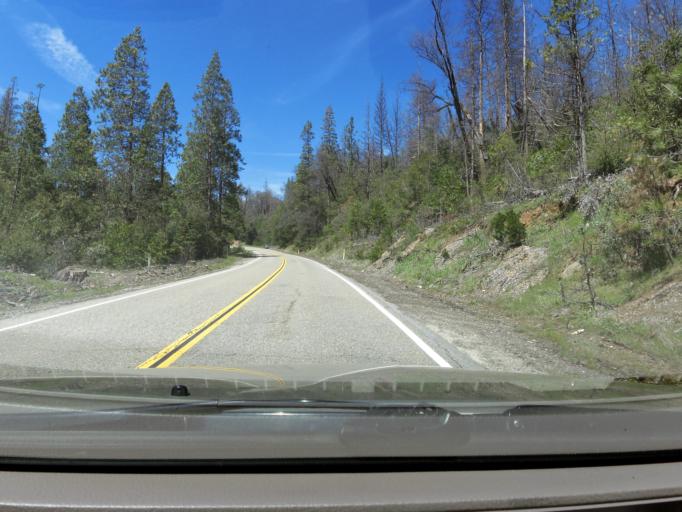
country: US
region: California
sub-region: Madera County
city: Oakhurst
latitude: 37.2846
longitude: -119.5768
